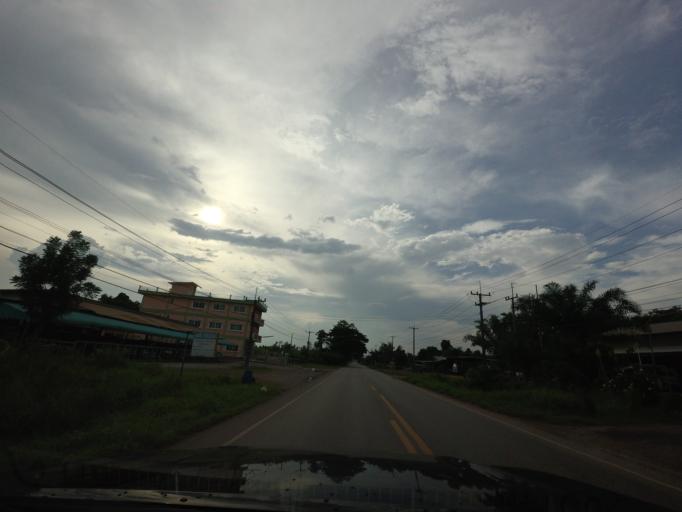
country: TH
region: Changwat Udon Thani
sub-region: Amphoe Ban Phue
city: Ban Phue
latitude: 17.6969
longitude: 102.4521
